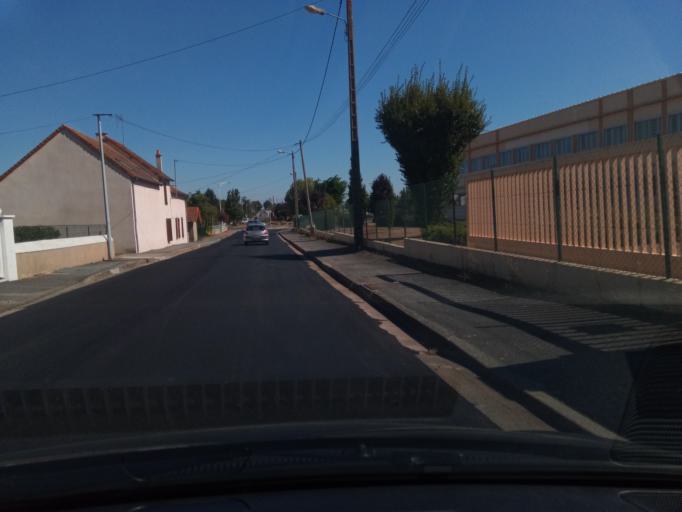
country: FR
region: Poitou-Charentes
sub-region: Departement de la Vienne
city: Montmorillon
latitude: 46.4300
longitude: 0.8792
